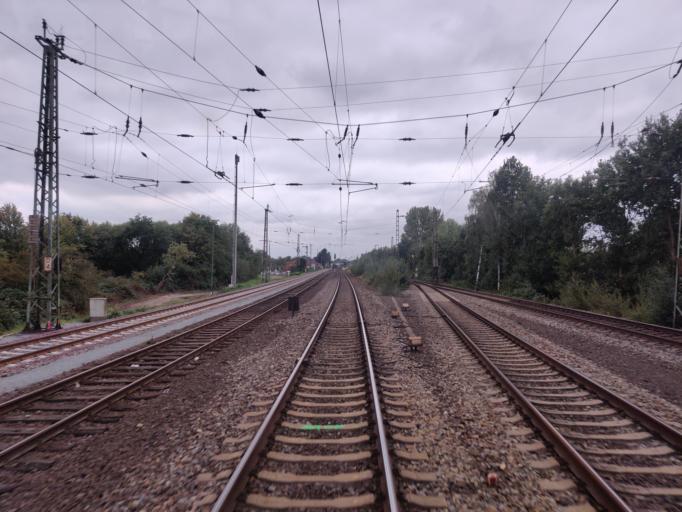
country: DE
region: Lower Saxony
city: Ritterhude
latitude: 53.1345
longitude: 8.7462
